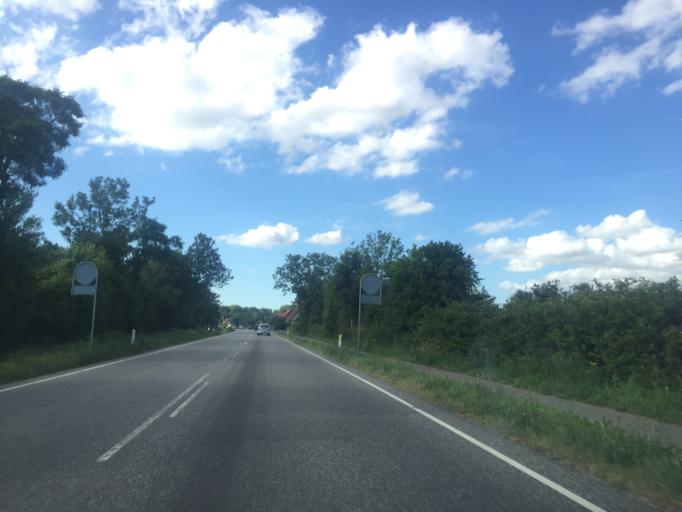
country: DK
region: Zealand
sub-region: Guldborgsund Kommune
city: Nykobing Falster
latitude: 54.7318
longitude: 11.9228
